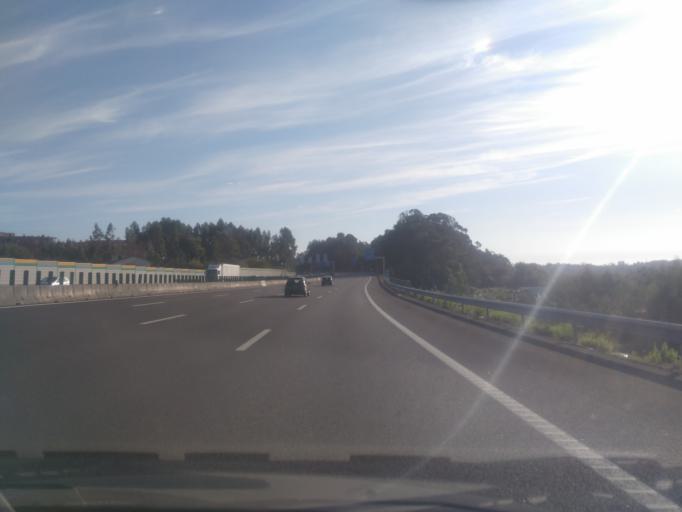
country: PT
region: Porto
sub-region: Vila Nova de Gaia
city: Grijo
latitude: 41.0240
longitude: -8.5762
